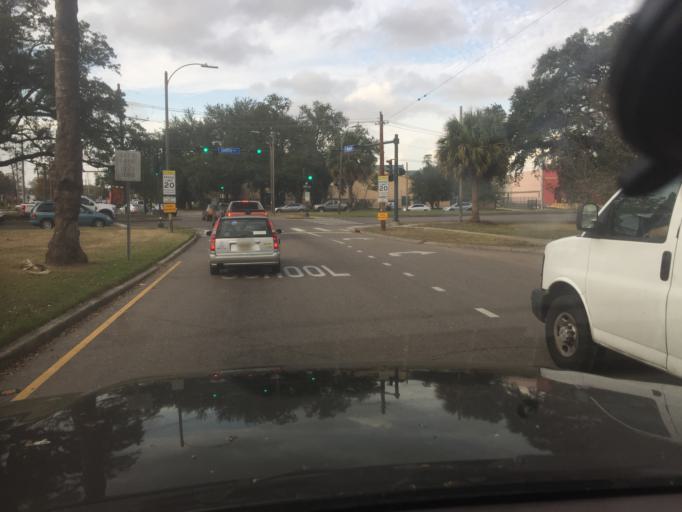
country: US
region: Louisiana
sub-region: Orleans Parish
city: New Orleans
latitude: 29.9880
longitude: -90.0743
